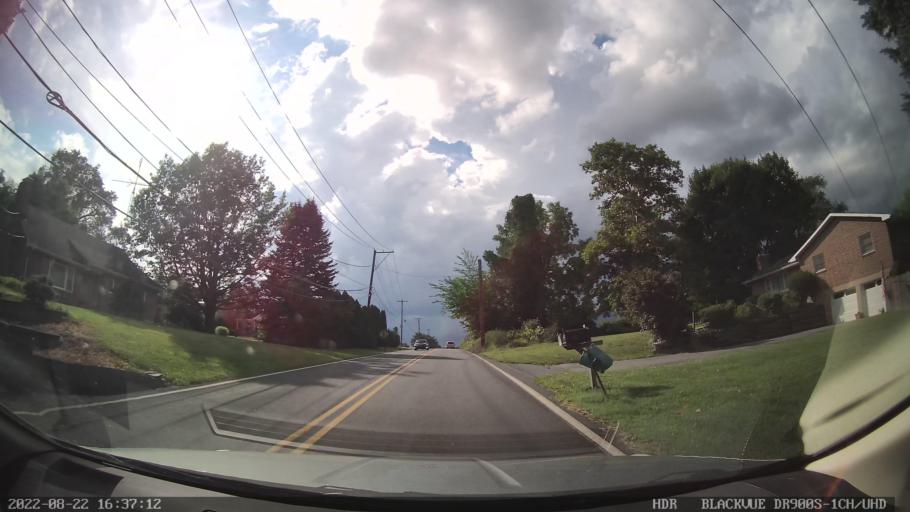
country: US
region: Pennsylvania
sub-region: Lehigh County
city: Dorneyville
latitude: 40.5639
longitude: -75.5320
